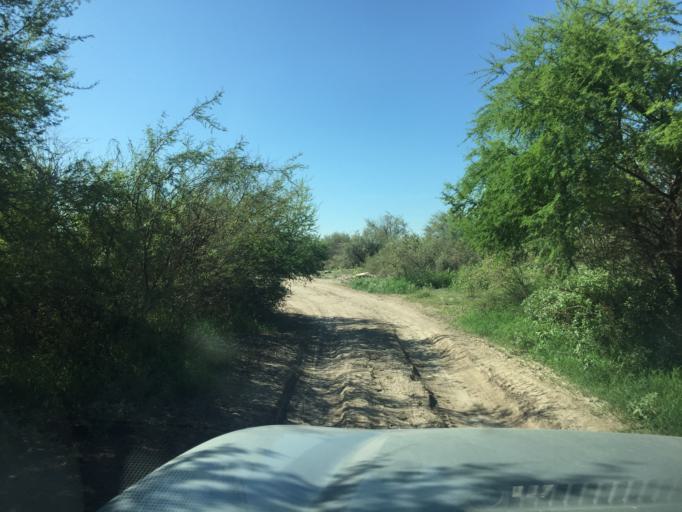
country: MX
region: Durango
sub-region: Gomez Palacio
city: San Felipe
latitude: 25.7316
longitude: -103.3736
